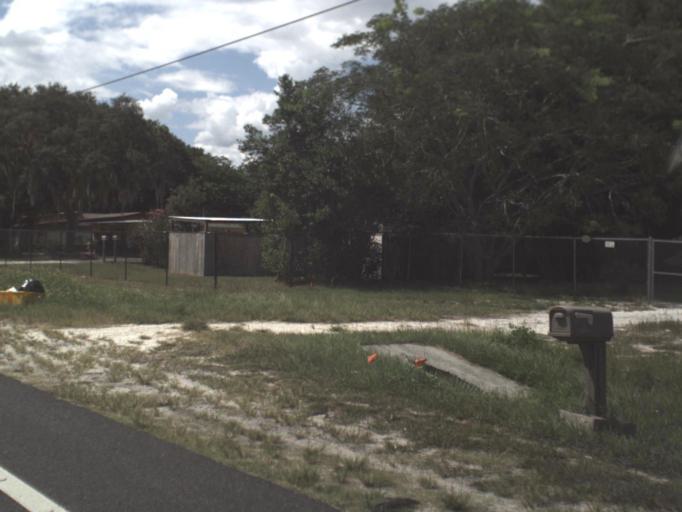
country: US
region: Florida
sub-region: Polk County
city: Wahneta
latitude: 27.9163
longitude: -81.7153
